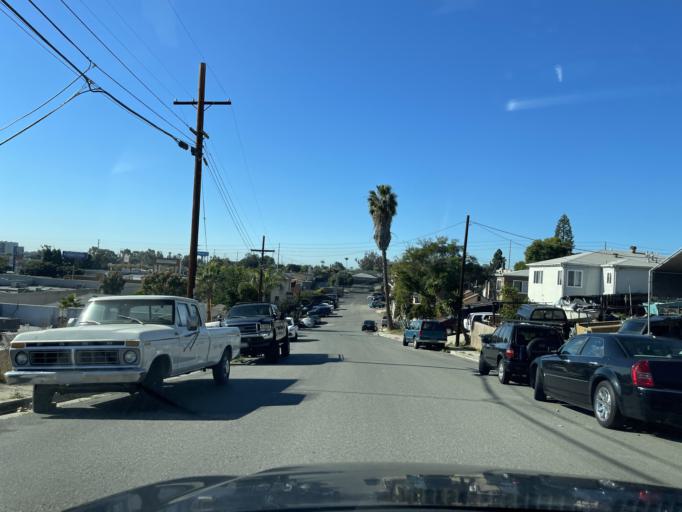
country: US
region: California
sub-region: San Diego County
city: National City
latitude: 32.6781
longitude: -117.0957
